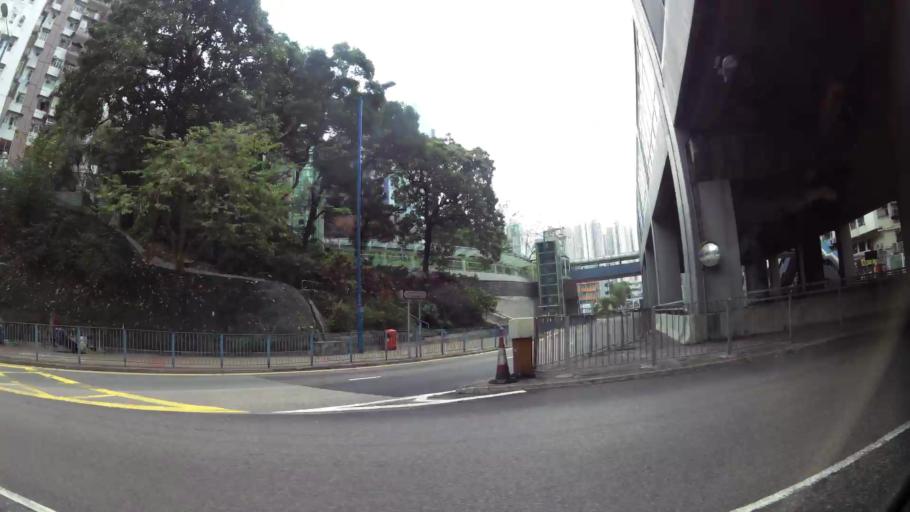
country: HK
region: Kowloon City
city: Kowloon
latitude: 22.3122
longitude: 114.2267
